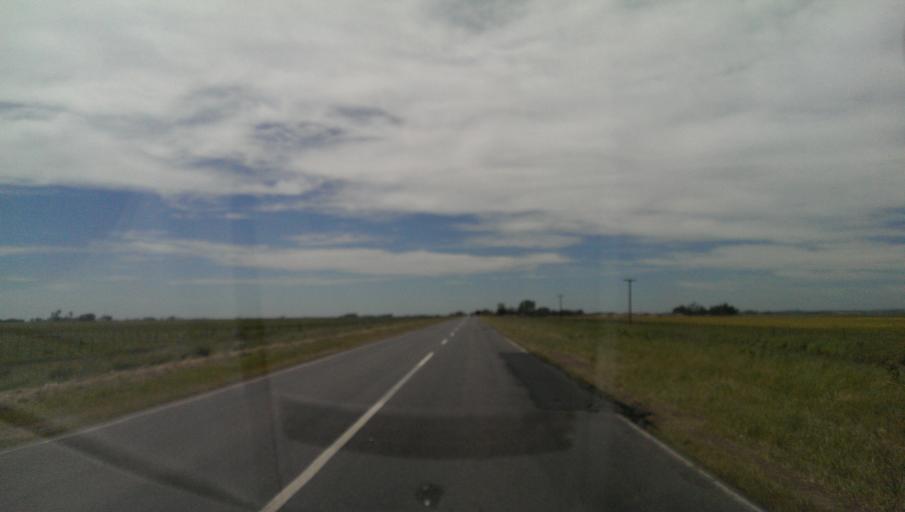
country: AR
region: Buenos Aires
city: Olavarria
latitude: -37.0419
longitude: -60.4372
